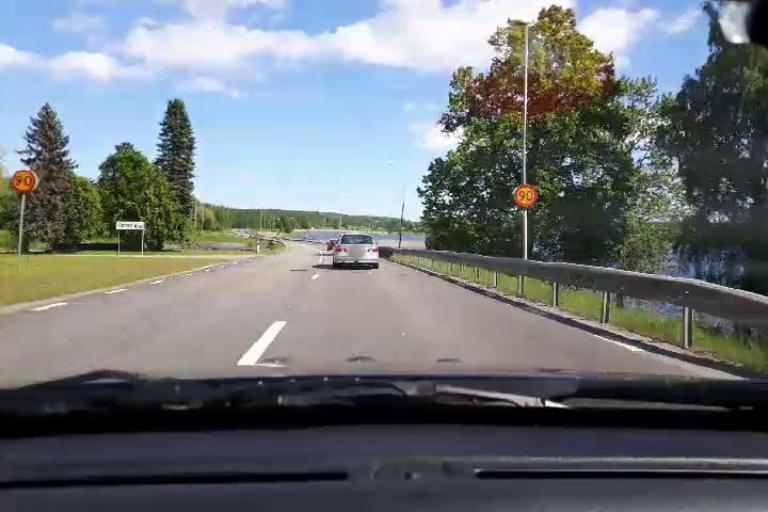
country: SE
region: Gaevleborg
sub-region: Hudiksvalls Kommun
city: Sorforsa
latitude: 61.7337
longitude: 16.9403
